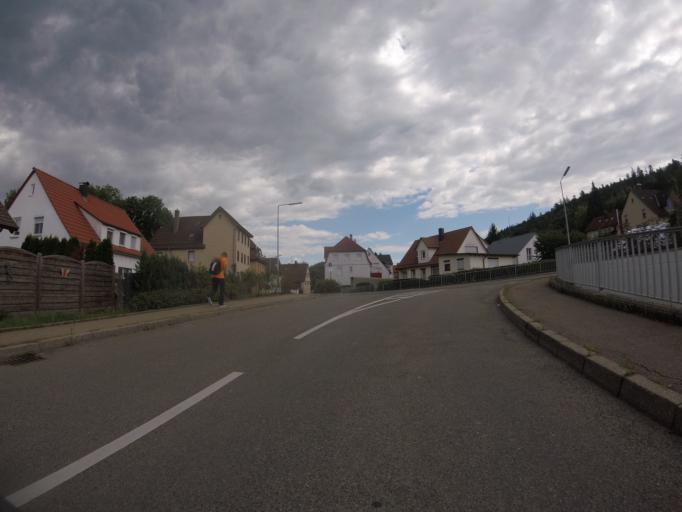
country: DE
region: Baden-Wuerttemberg
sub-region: Regierungsbezirk Stuttgart
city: Lorch
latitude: 48.7964
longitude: 9.6853
